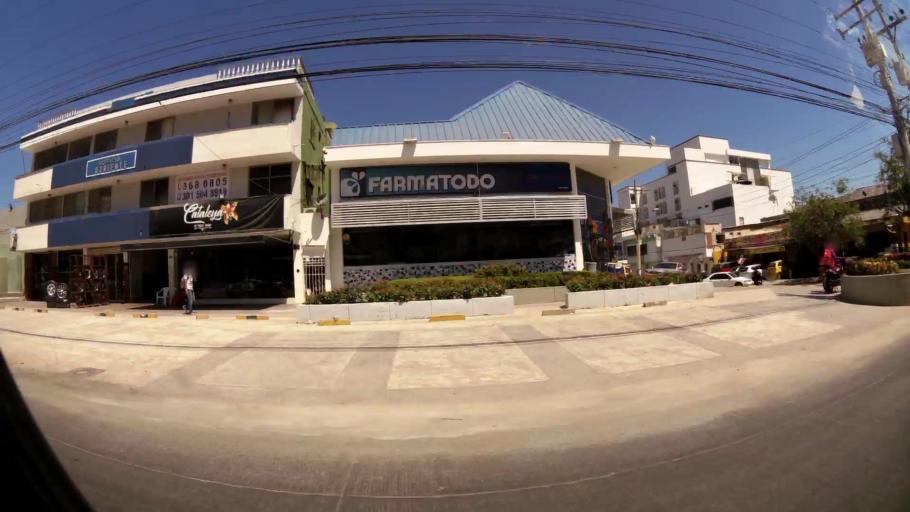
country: CO
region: Atlantico
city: Barranquilla
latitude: 10.9936
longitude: -74.8104
